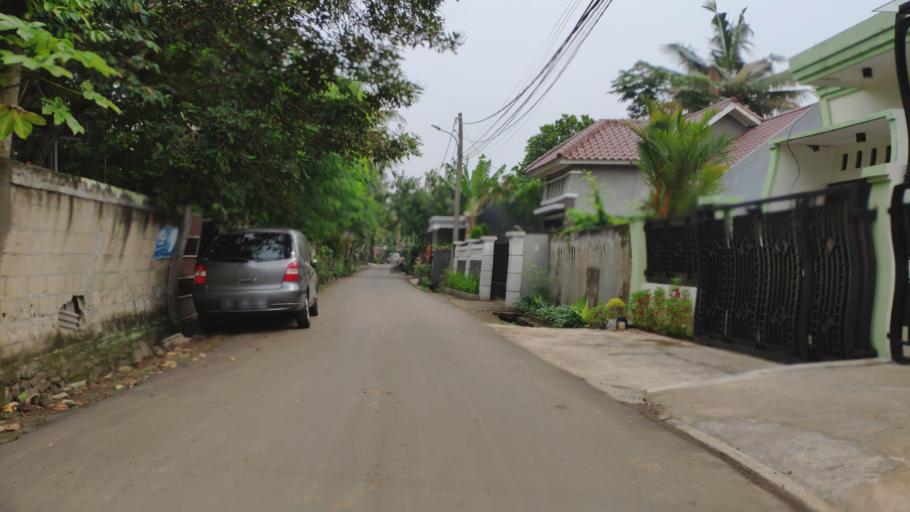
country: ID
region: West Java
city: Depok
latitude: -6.3530
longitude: 106.7952
